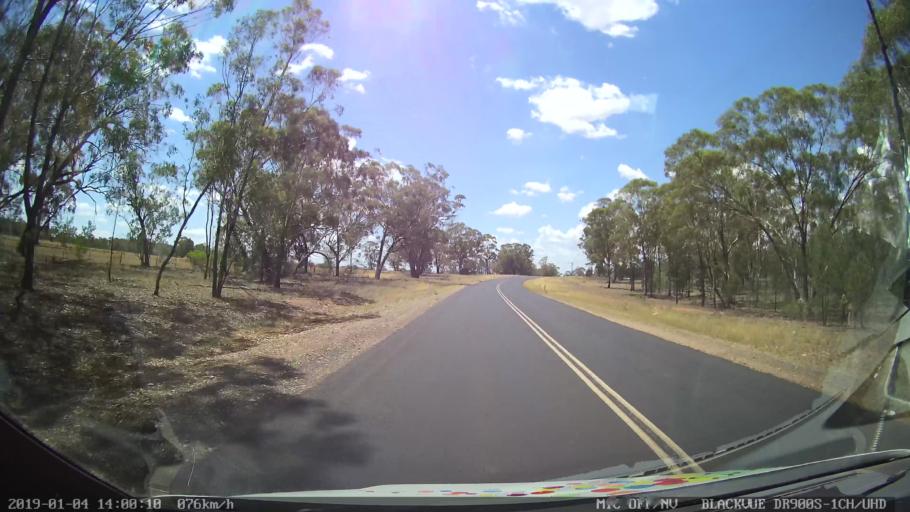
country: AU
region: New South Wales
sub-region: Dubbo Municipality
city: Dubbo
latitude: -32.3090
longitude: 148.5905
